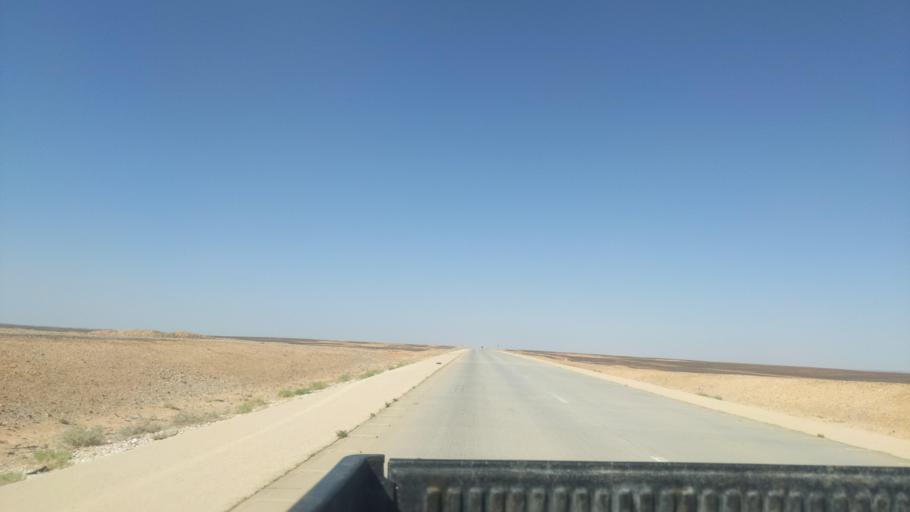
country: JO
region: Amman
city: Al Azraq ash Shamali
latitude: 31.4342
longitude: 36.7429
